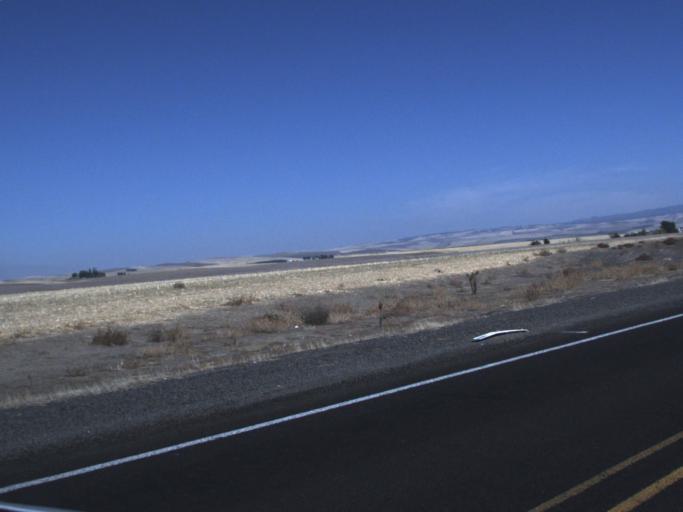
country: US
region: Washington
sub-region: Walla Walla County
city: Walla Walla
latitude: 46.0855
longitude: -118.3580
